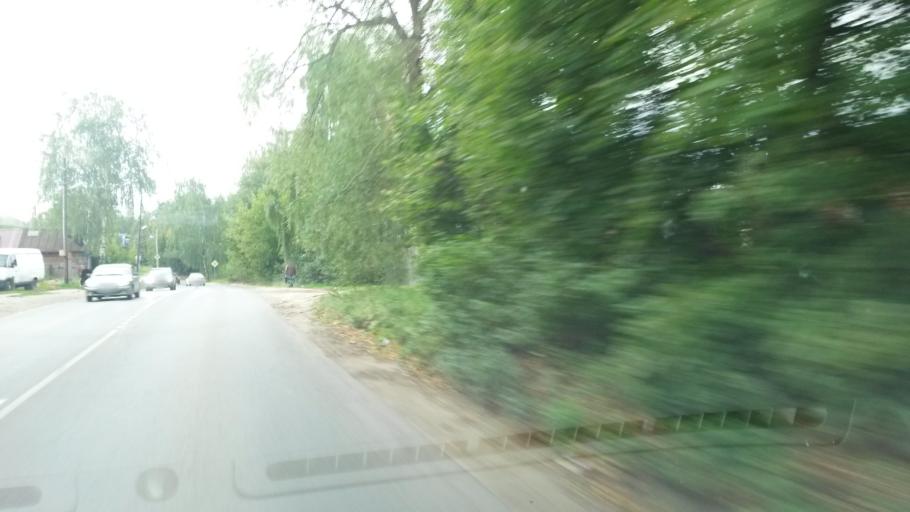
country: RU
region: Ivanovo
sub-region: Gorod Ivanovo
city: Ivanovo
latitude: 57.0272
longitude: 40.9336
